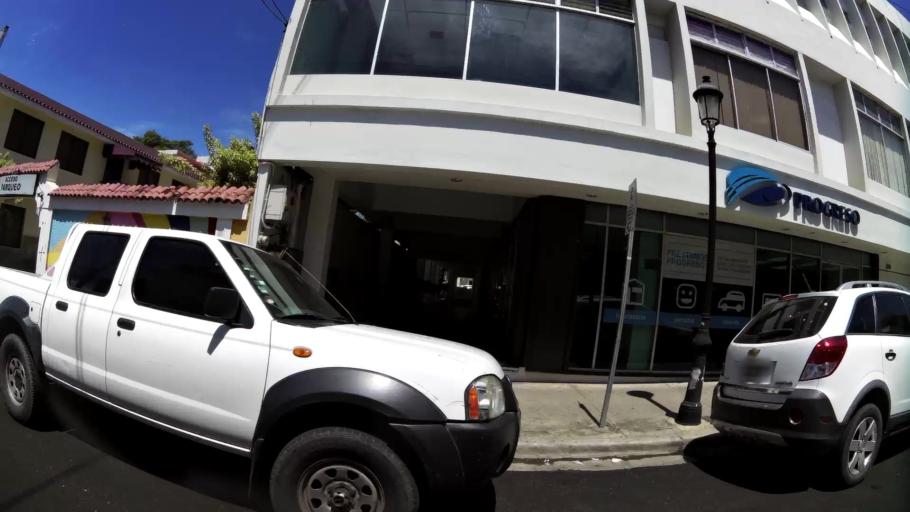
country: DO
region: Santiago
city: Santiago de los Caballeros
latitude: 19.4506
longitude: -70.7005
